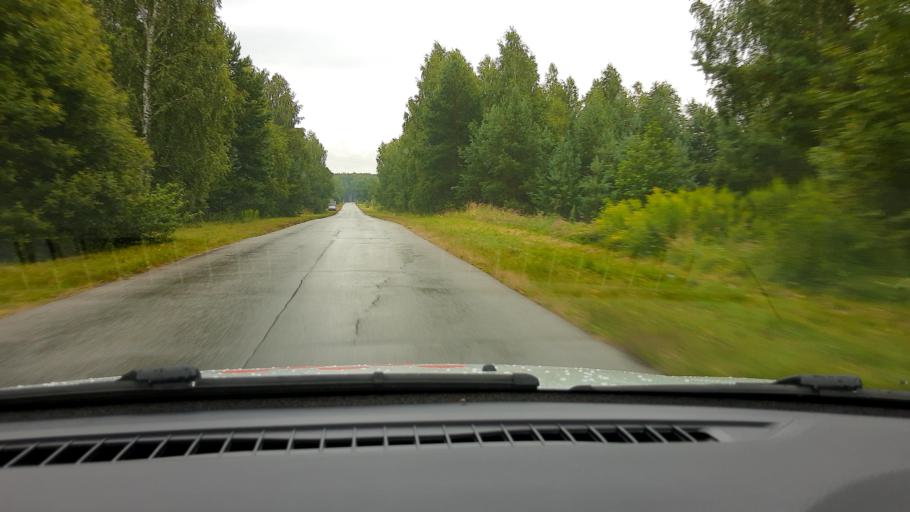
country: RU
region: Nizjnij Novgorod
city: Dal'neye Konstantinovo
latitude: 55.9498
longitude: 43.9683
